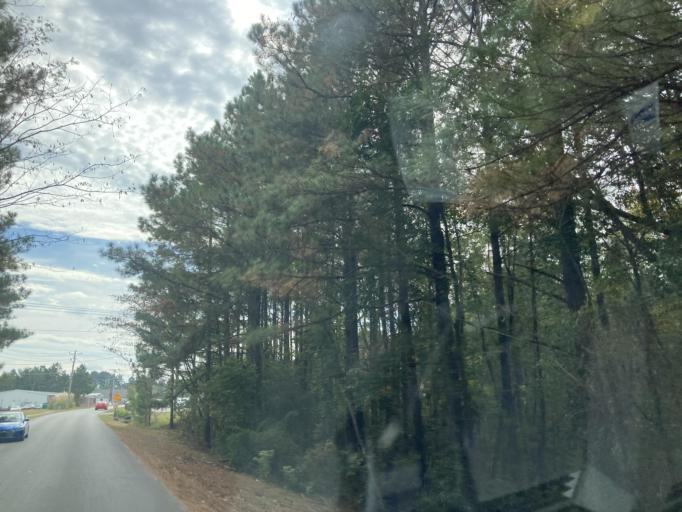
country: US
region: Mississippi
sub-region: Lamar County
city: West Hattiesburg
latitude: 31.3261
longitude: -89.4148
